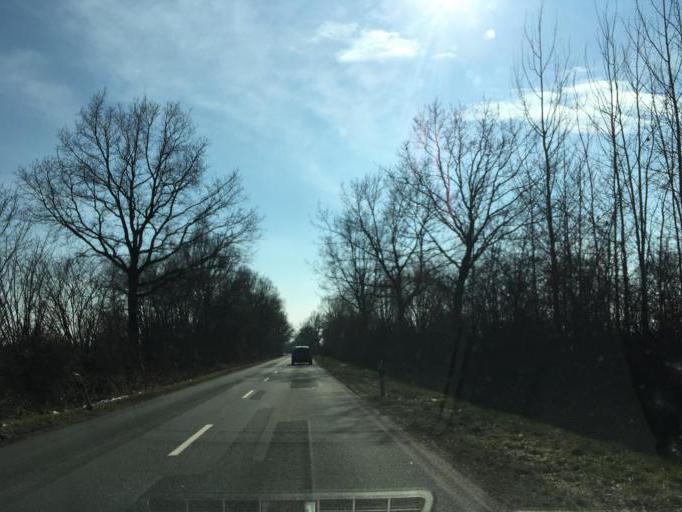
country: DE
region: Schleswig-Holstein
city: Escheburg
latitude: 53.4808
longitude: 10.3170
